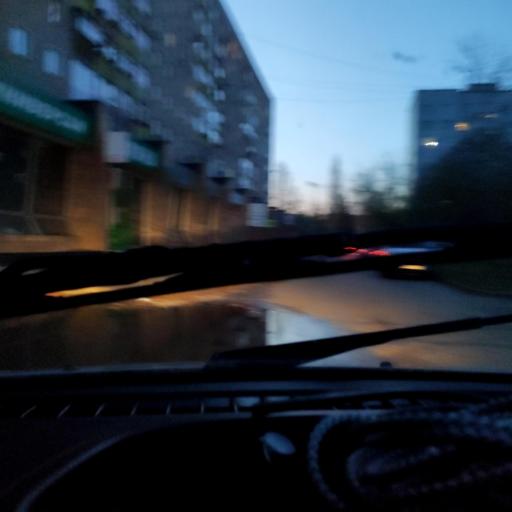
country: RU
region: Samara
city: Tol'yatti
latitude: 53.5104
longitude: 49.4459
